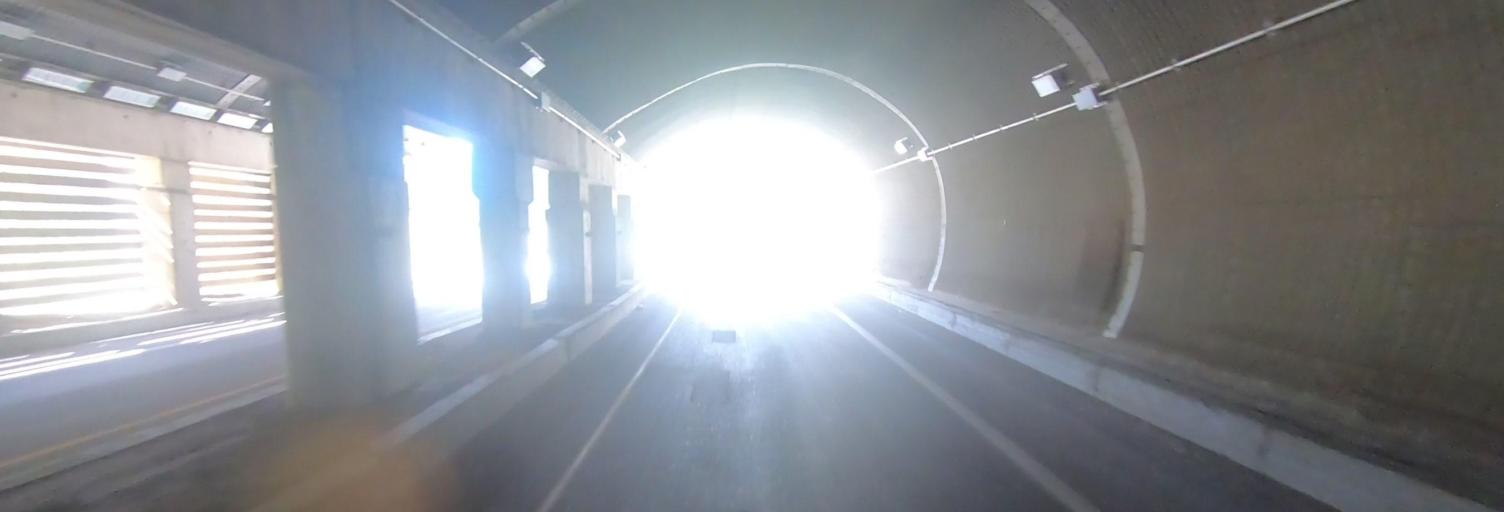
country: CA
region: British Columbia
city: Golden
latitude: 51.3270
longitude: -117.4718
